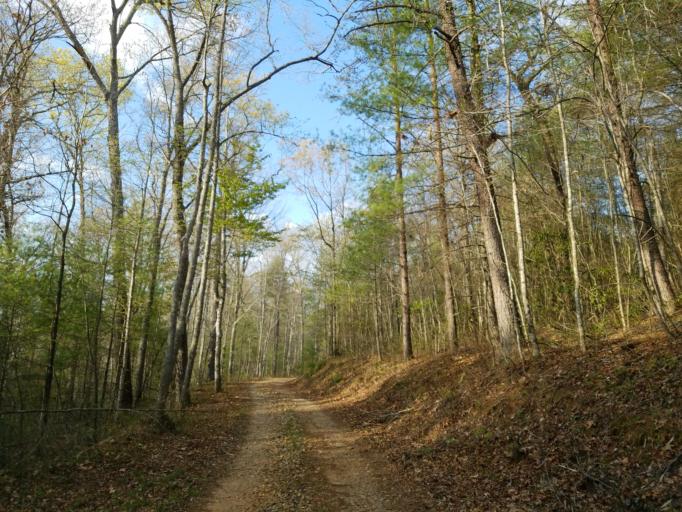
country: US
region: Georgia
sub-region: Fannin County
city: Blue Ridge
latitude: 34.7214
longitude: -84.2009
